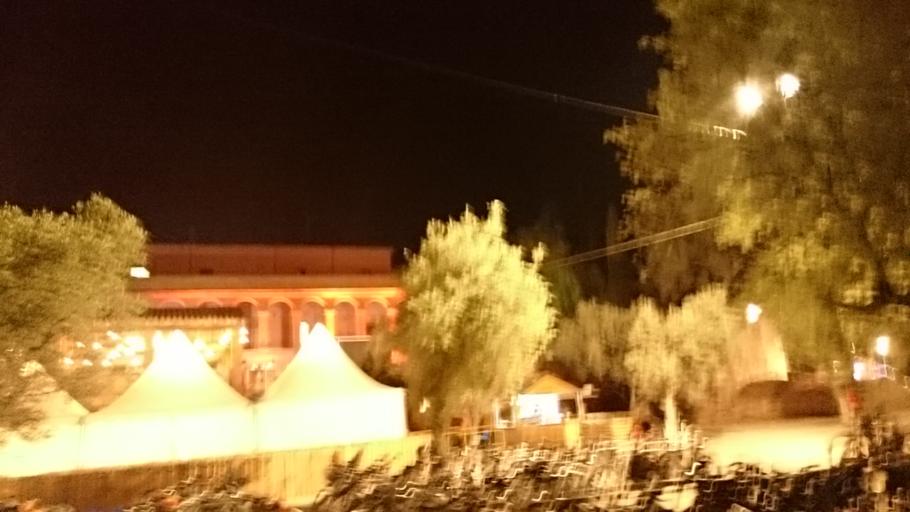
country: ES
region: Catalonia
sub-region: Provincia de Barcelona
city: Vilanova i la Geltru
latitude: 41.2407
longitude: 1.7161
